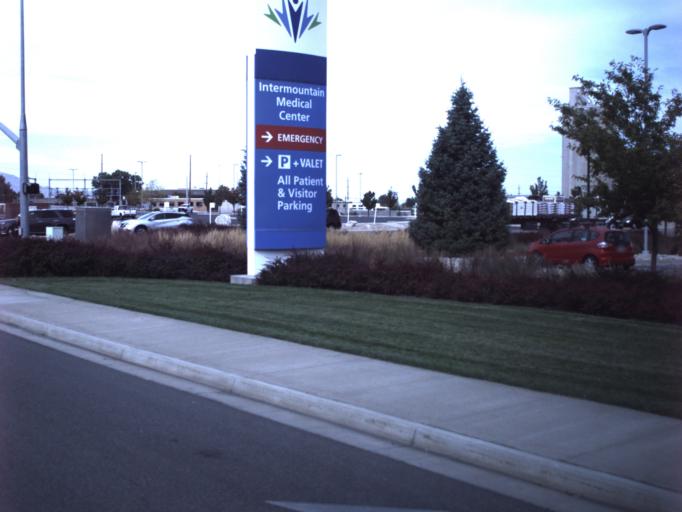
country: US
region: Utah
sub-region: Salt Lake County
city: Murray
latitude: 40.6559
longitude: -111.8936
